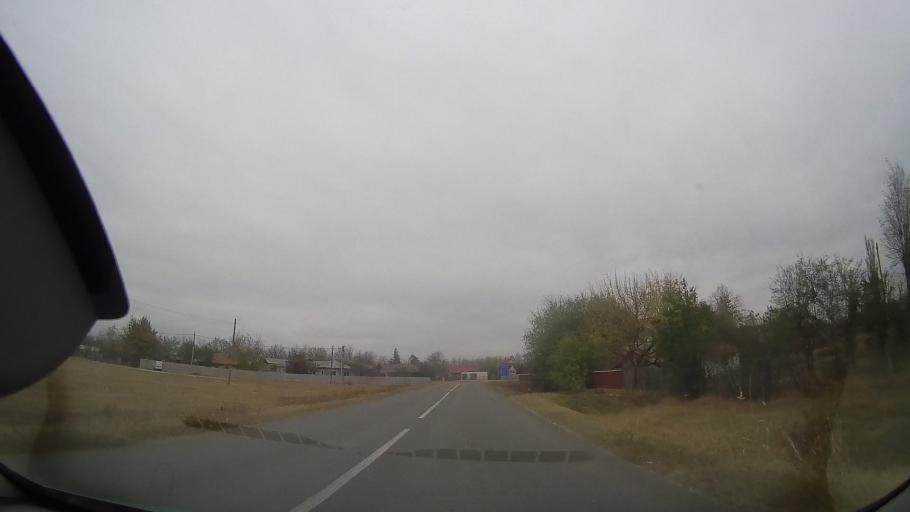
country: RO
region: Ialomita
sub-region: Comuna Grivita
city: Grivita
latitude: 44.7308
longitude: 27.2998
